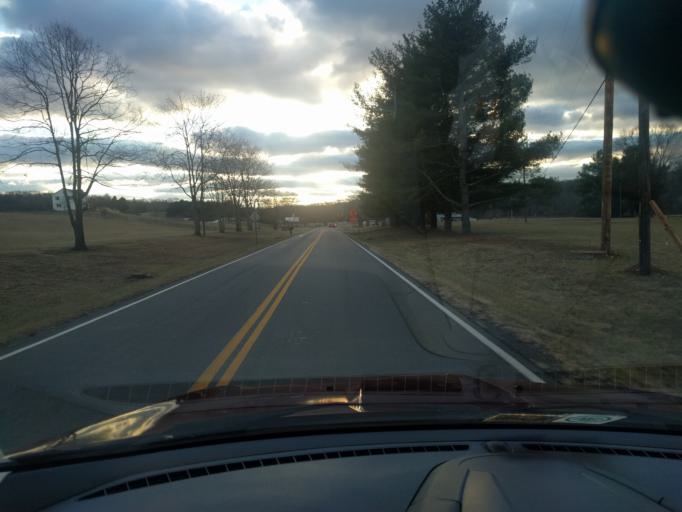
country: US
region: Virginia
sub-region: City of Bedford
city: Bedford
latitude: 37.3924
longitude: -79.5546
